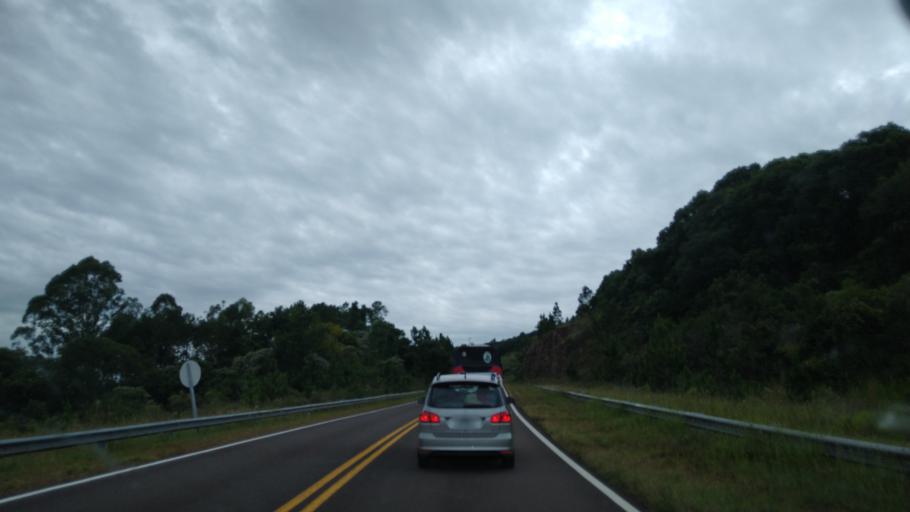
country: AR
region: Misiones
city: Bernardo de Irigoyen
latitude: -26.3215
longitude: -53.7498
